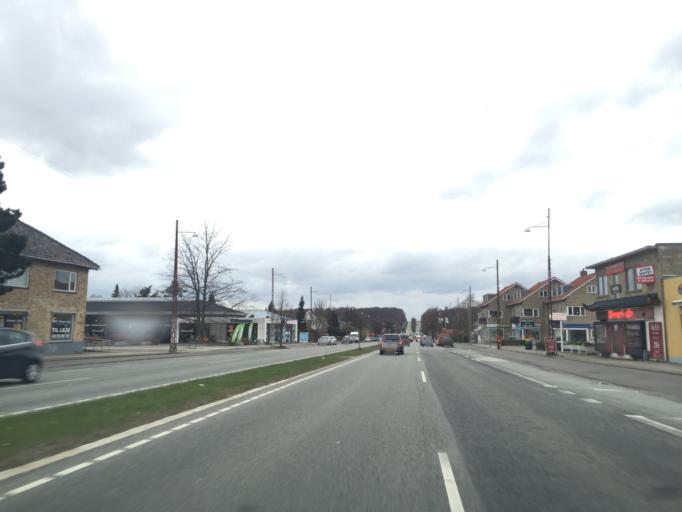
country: DK
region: Capital Region
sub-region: Rudersdal Kommune
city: Holte
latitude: 55.7935
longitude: 12.4844
